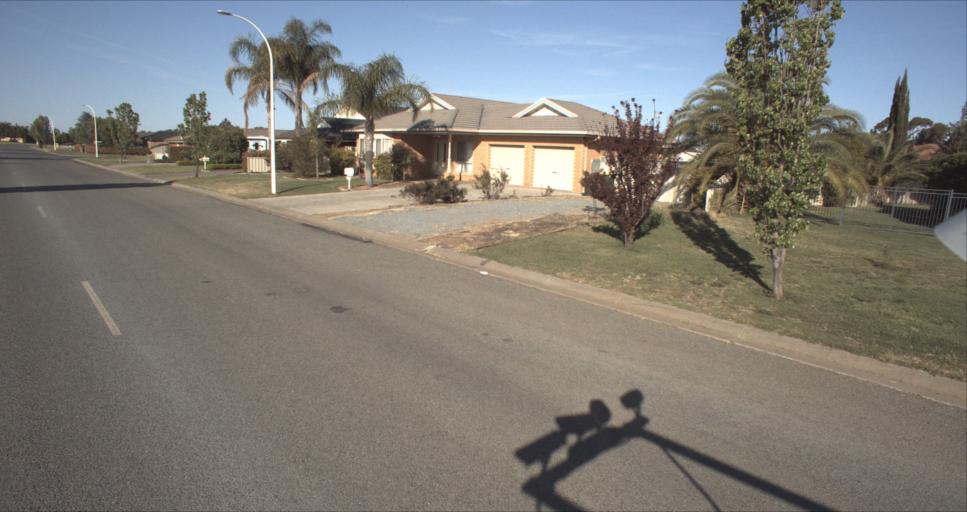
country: AU
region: New South Wales
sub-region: Leeton
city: Leeton
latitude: -34.5404
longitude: 146.4015
